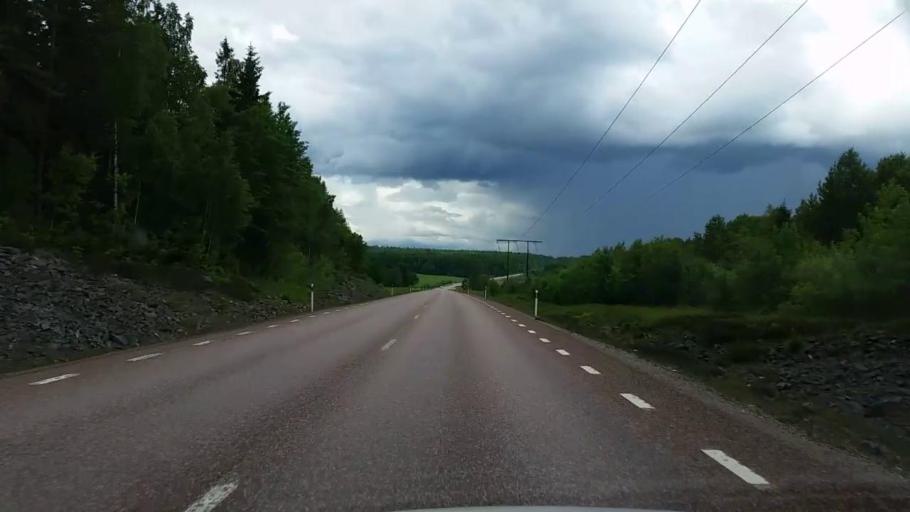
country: SE
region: Gaevleborg
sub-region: Hofors Kommun
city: Hofors
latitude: 60.5330
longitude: 16.4580
